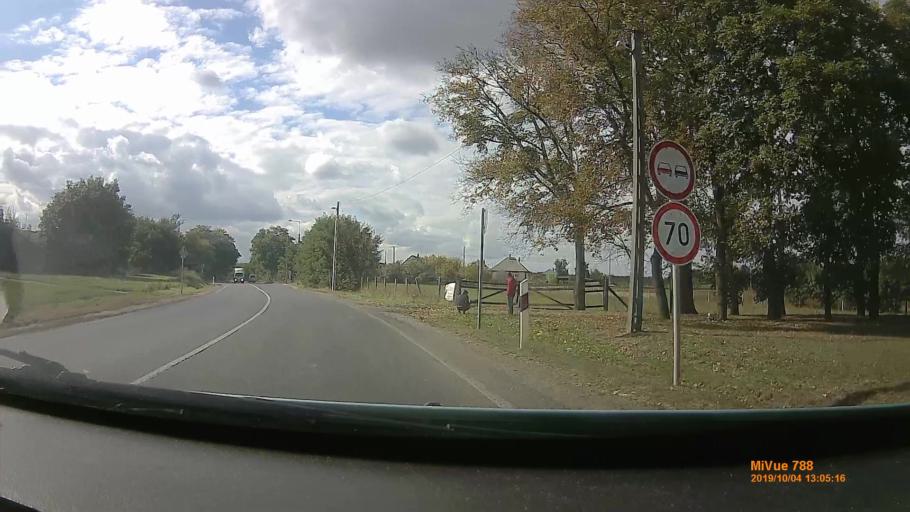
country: HU
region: Szabolcs-Szatmar-Bereg
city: Nyirtelek
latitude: 47.9600
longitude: 21.6151
